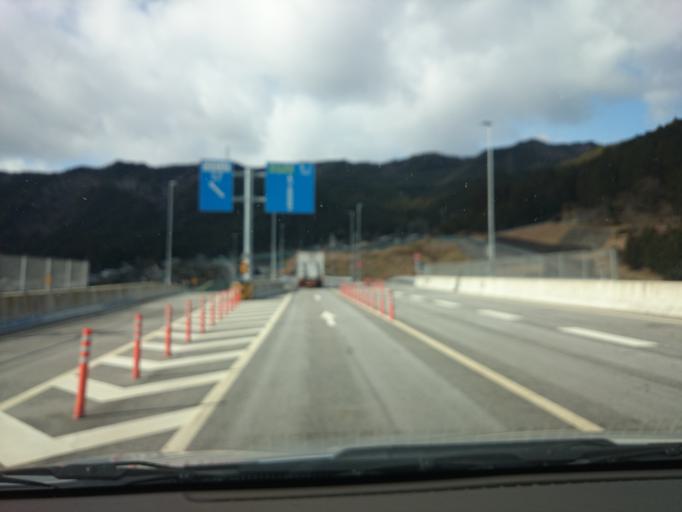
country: JP
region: Gifu
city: Gujo
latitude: 35.7448
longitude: 137.1490
